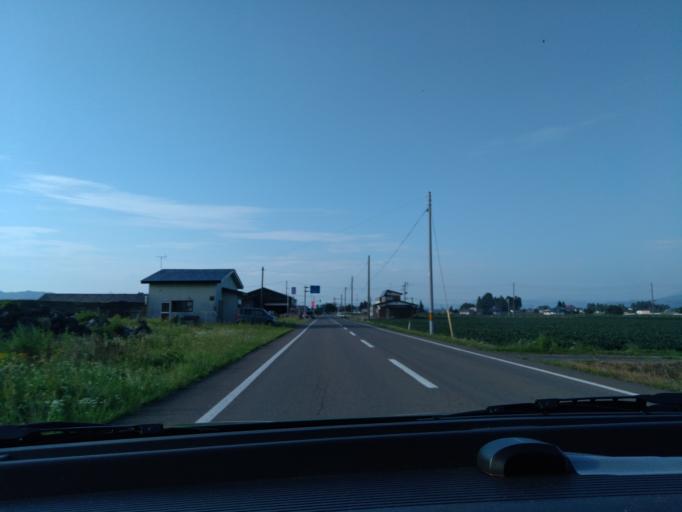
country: JP
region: Akita
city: Omagari
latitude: 39.4987
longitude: 140.5597
